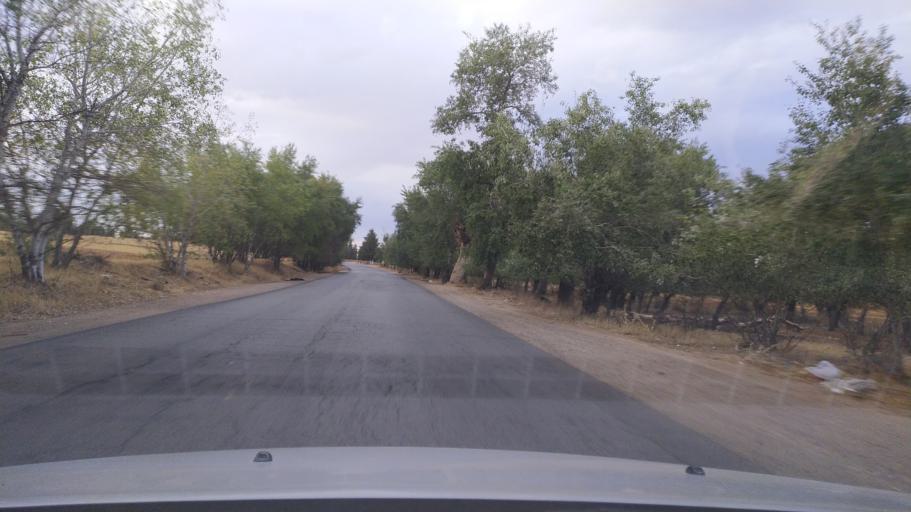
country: DZ
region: Tiaret
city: Frenda
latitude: 35.0400
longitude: 1.0894
